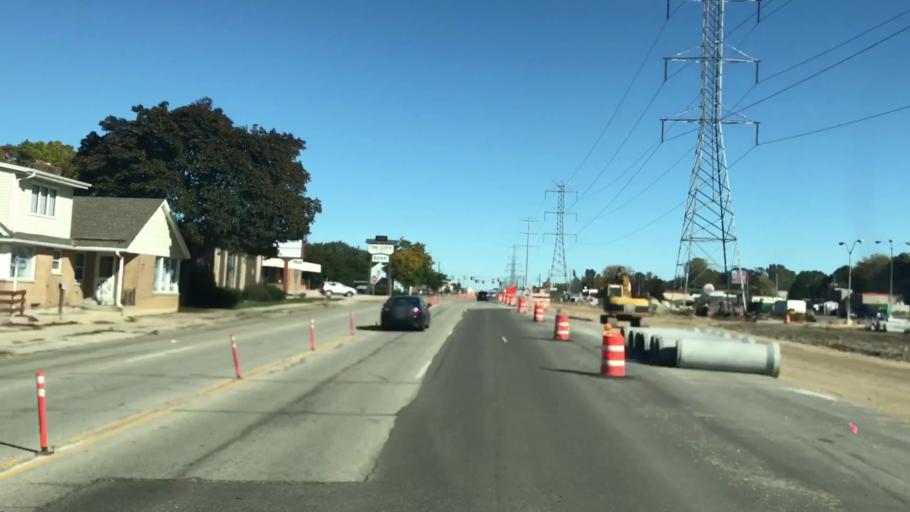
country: US
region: Wisconsin
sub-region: Milwaukee County
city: Hales Corners
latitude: 42.9417
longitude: -88.0484
